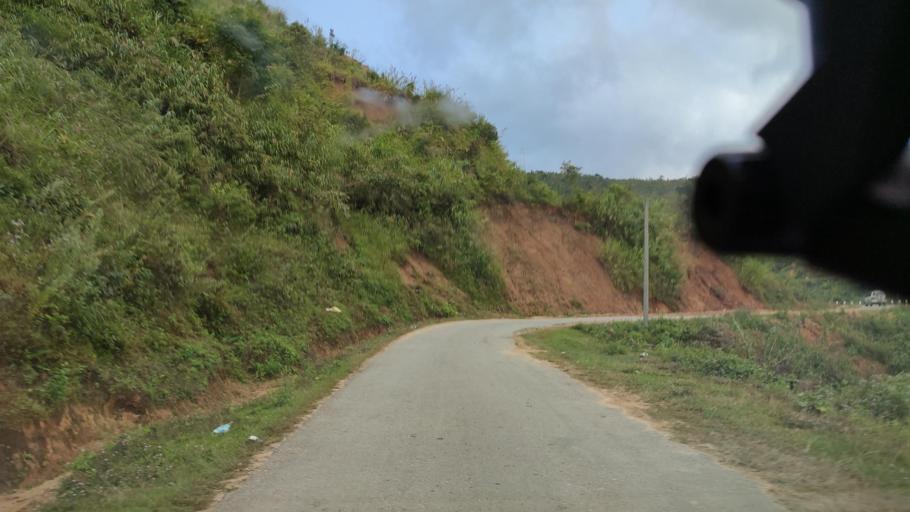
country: TH
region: Chiang Rai
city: Mae Sai
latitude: 21.2182
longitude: 99.6218
